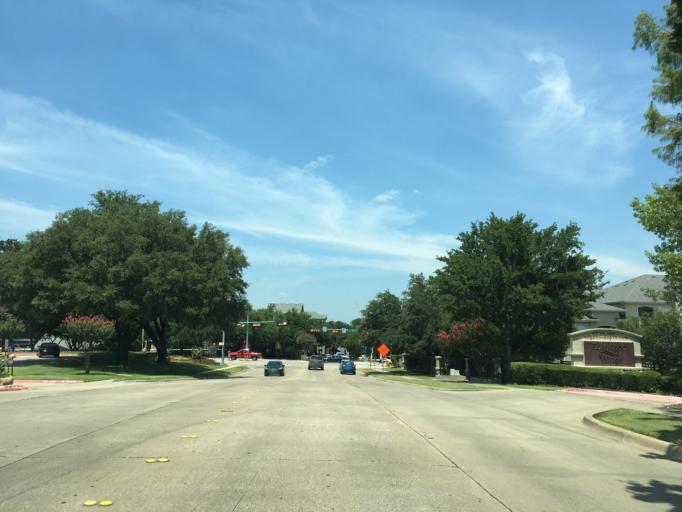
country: US
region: Texas
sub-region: Denton County
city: Lewisville
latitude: 33.0129
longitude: -96.9878
